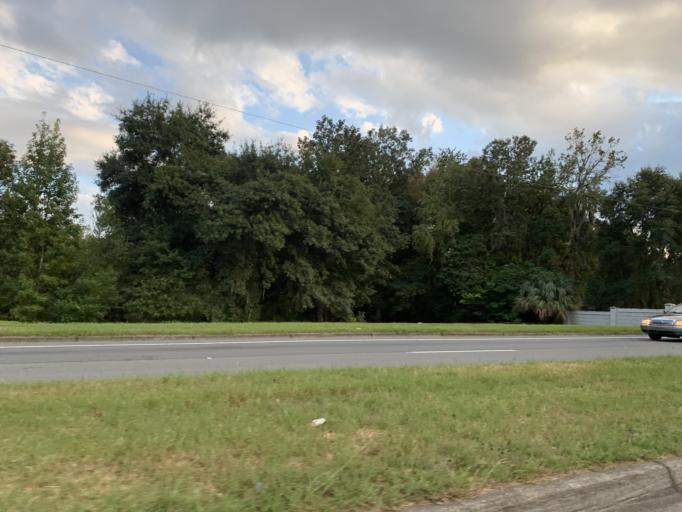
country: US
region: Florida
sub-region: Marion County
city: Ocala
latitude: 29.1541
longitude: -82.1499
